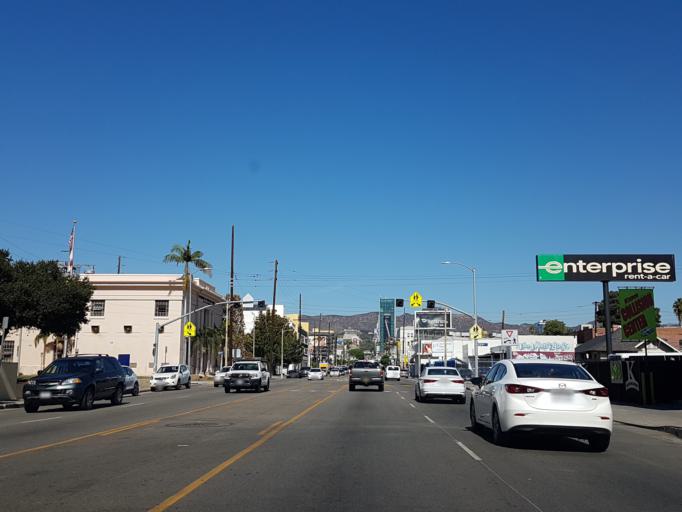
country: US
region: California
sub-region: Los Angeles County
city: Hollywood
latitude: 34.0883
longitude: -118.3266
